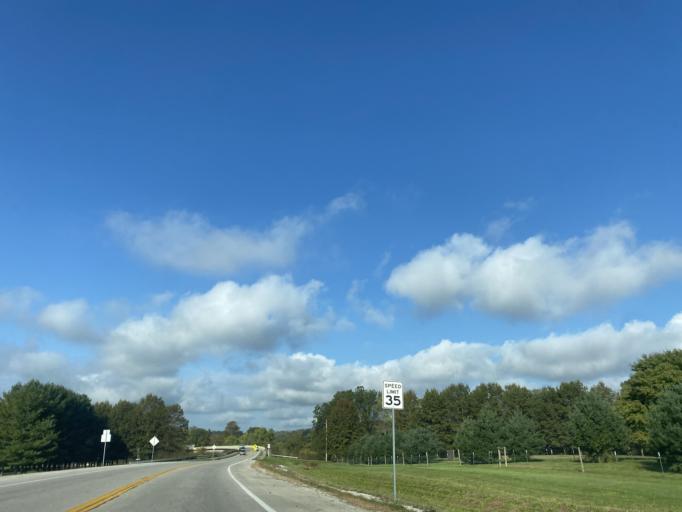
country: US
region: Kentucky
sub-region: Pendleton County
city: Falmouth
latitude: 38.6774
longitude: -84.3237
